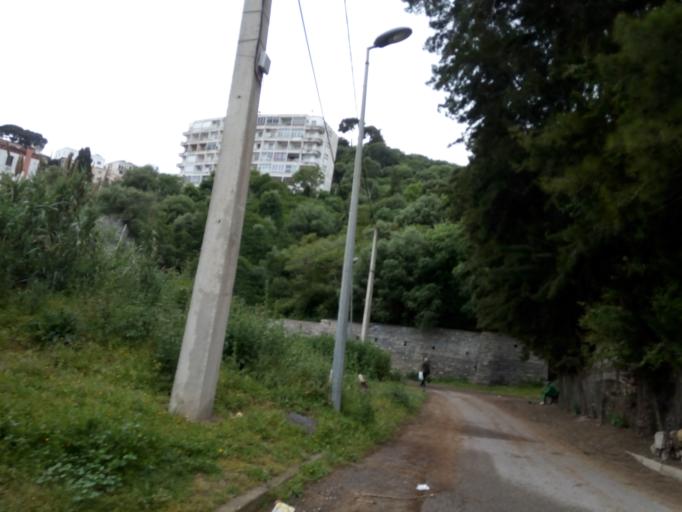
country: DZ
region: Alger
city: Algiers
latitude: 36.7641
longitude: 3.0410
